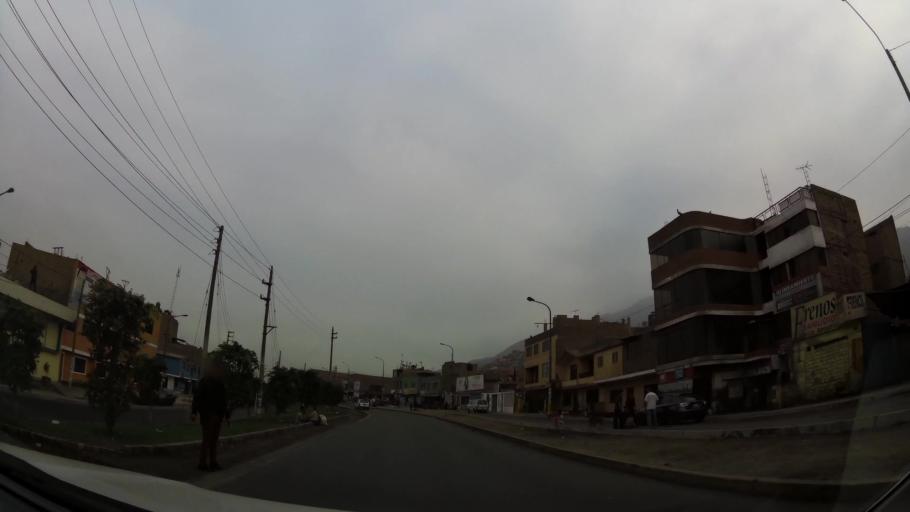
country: PE
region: Lima
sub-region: Lima
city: Independencia
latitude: -11.9857
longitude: -77.0157
